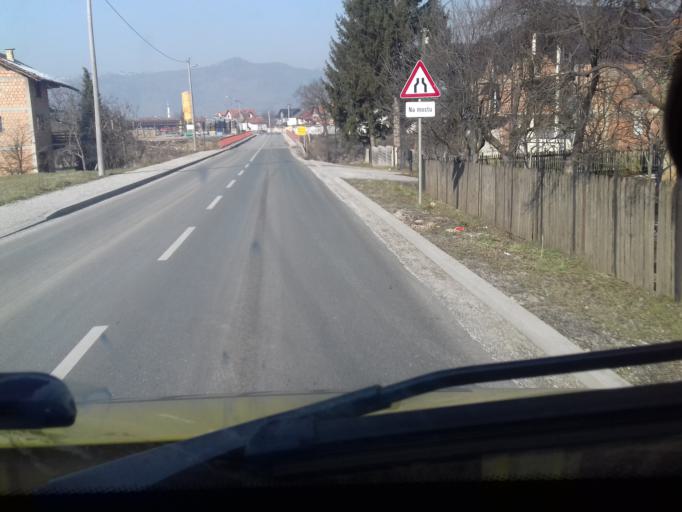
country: BA
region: Federation of Bosnia and Herzegovina
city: Ilijas
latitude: 43.9339
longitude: 18.2995
